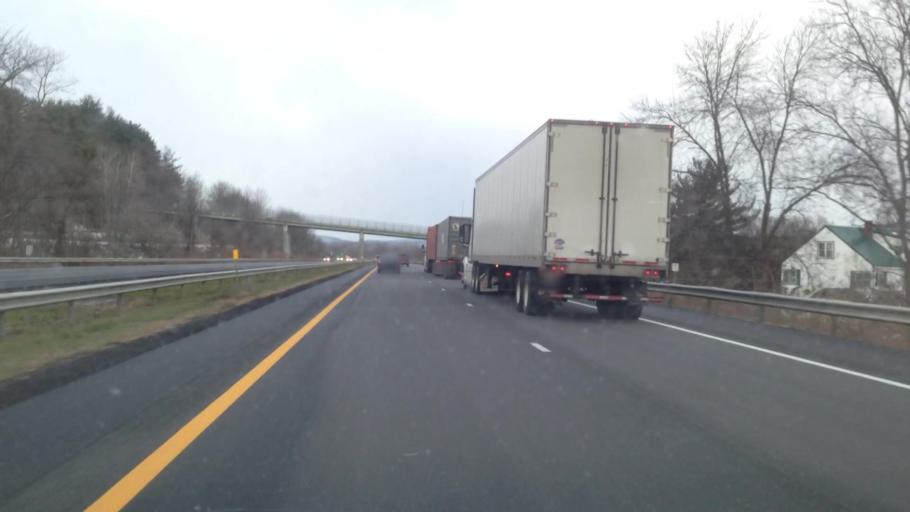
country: US
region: New York
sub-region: Montgomery County
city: Fonda
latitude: 42.9400
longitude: -74.3393
